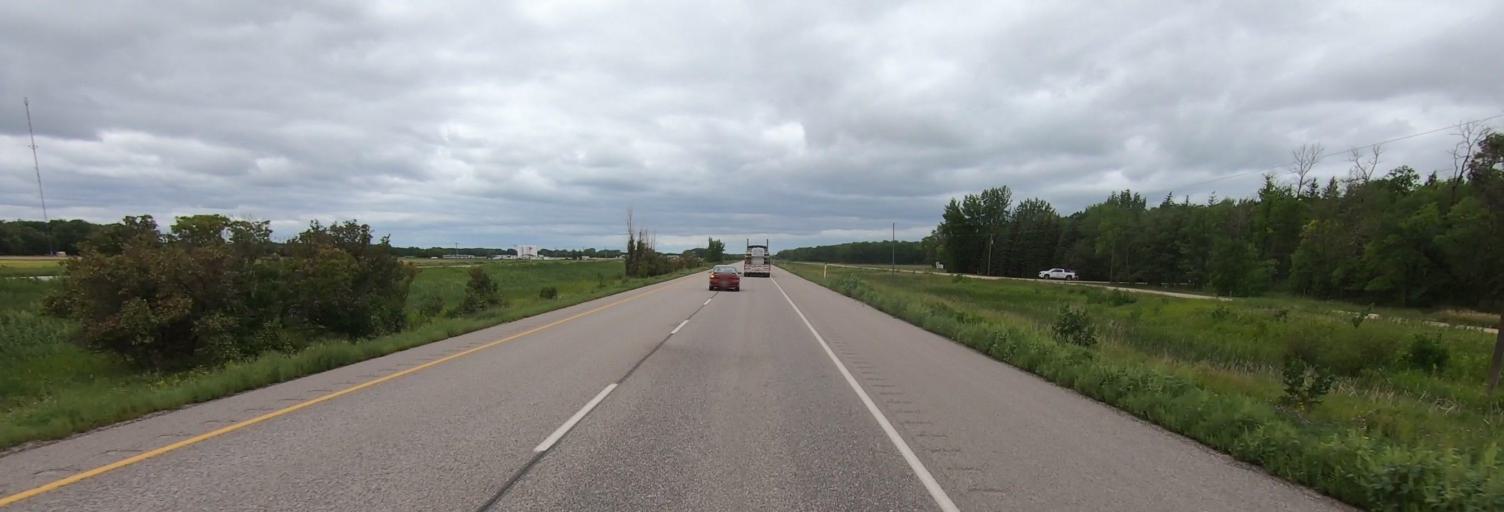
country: CA
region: Manitoba
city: Portage la Prairie
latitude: 49.9739
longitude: -98.1632
